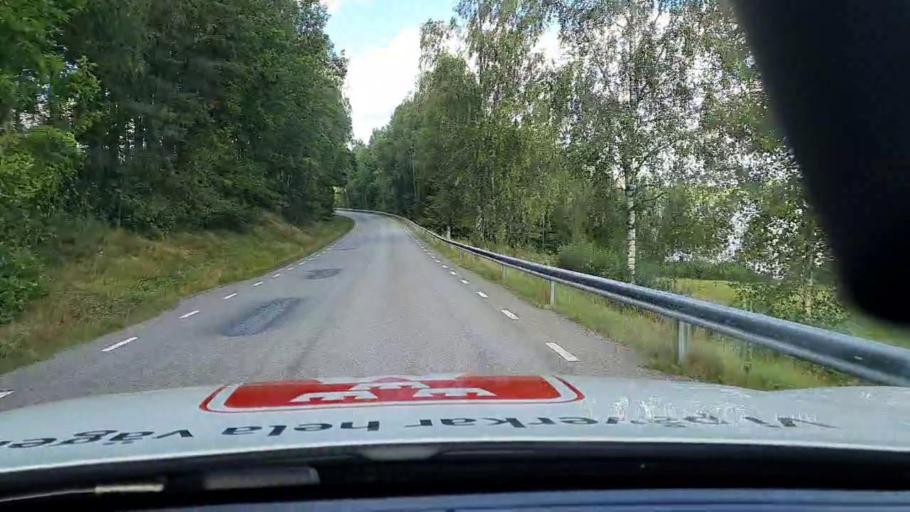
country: SE
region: Vaestra Goetaland
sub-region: Marks Kommun
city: Fritsla
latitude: 57.3651
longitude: 12.8652
